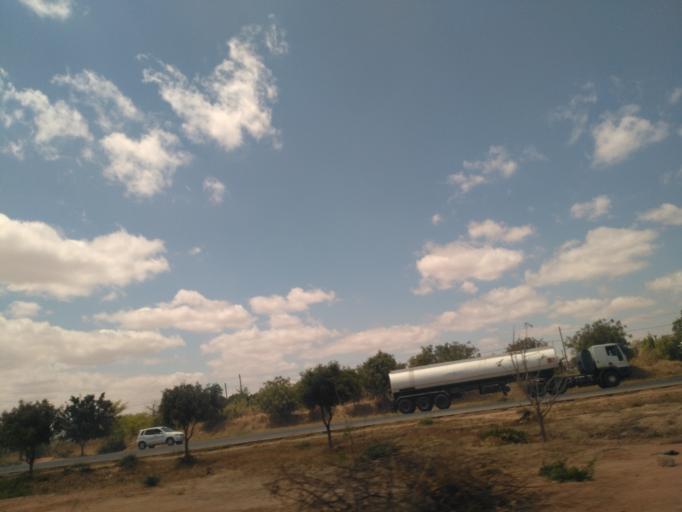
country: TZ
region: Dodoma
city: Kisasa
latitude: -6.1605
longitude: 35.7939
